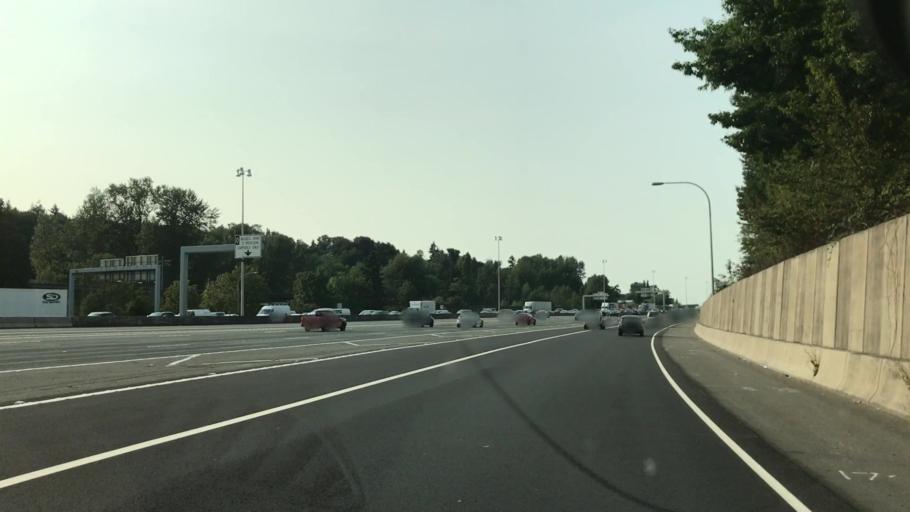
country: US
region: Washington
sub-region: King County
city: Tukwila
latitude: 47.4670
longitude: -122.2668
